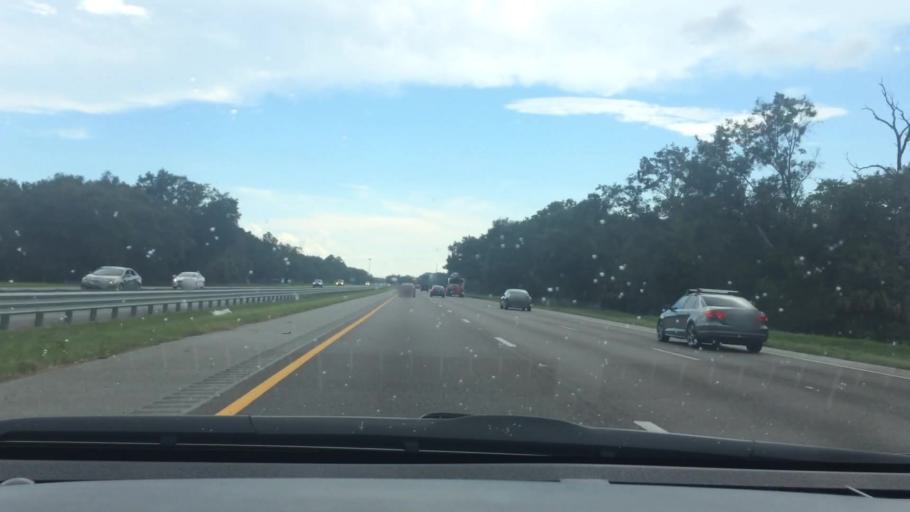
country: US
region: Florida
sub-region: Hillsborough County
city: University
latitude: 28.1043
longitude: -82.4387
